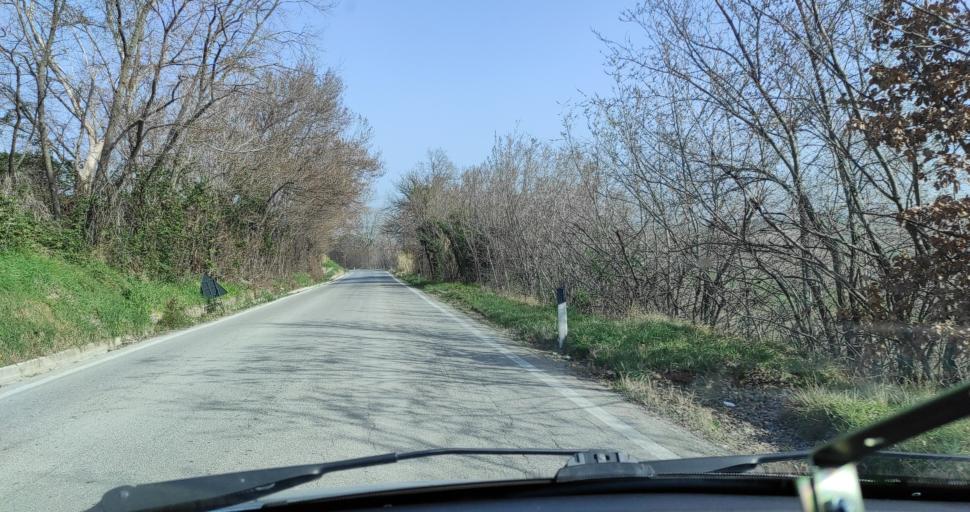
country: IT
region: The Marches
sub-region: Provincia di Macerata
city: Loro Piceno
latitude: 43.1697
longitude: 13.4250
